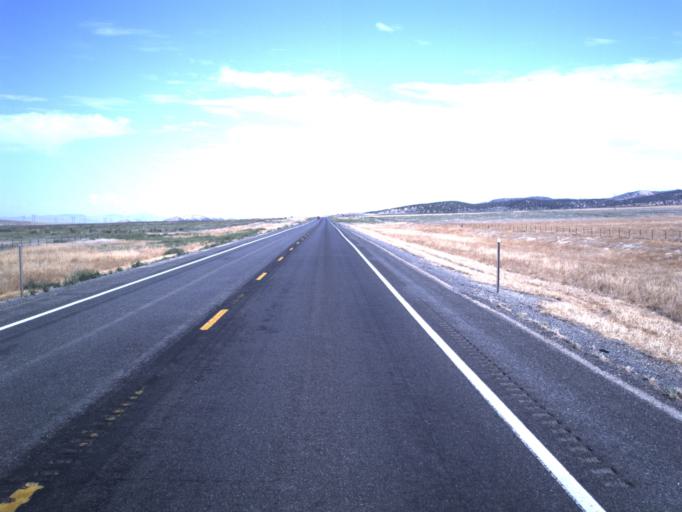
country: US
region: Utah
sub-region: Sanpete County
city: Gunnison
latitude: 39.2996
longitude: -111.8929
